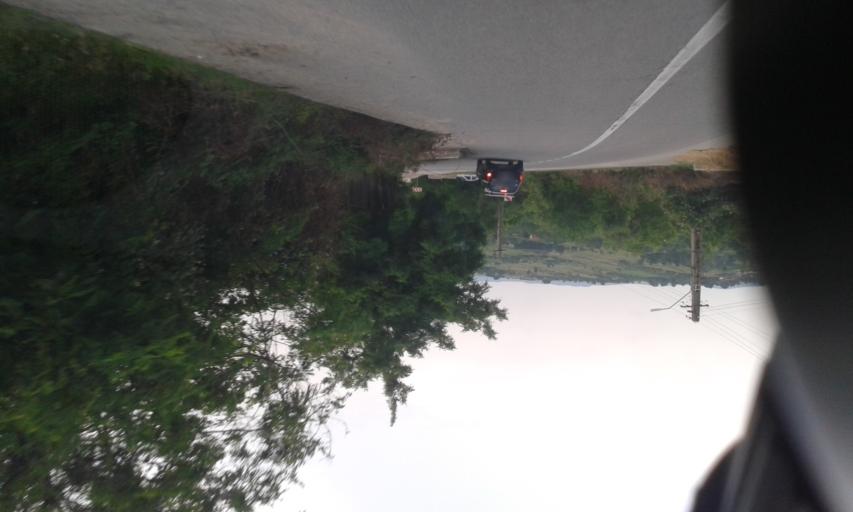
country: RO
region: Gorj
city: Novaci-Straini
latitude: 45.1862
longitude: 23.6819
